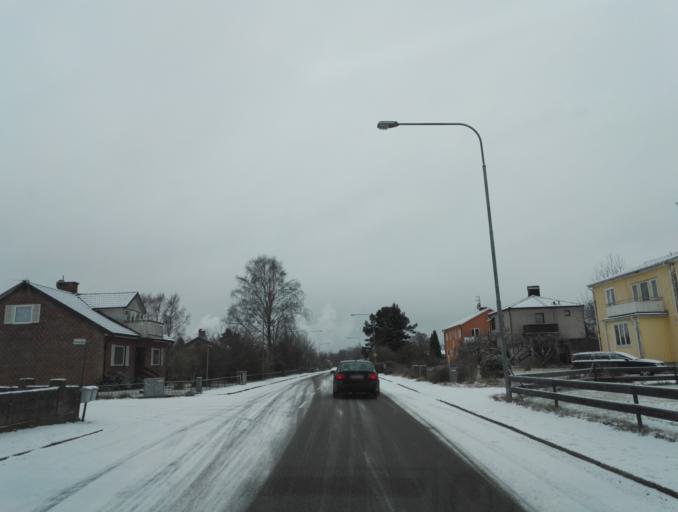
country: SE
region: Kronoberg
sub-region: Lessebo Kommun
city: Lessebo
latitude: 56.7534
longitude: 15.2804
